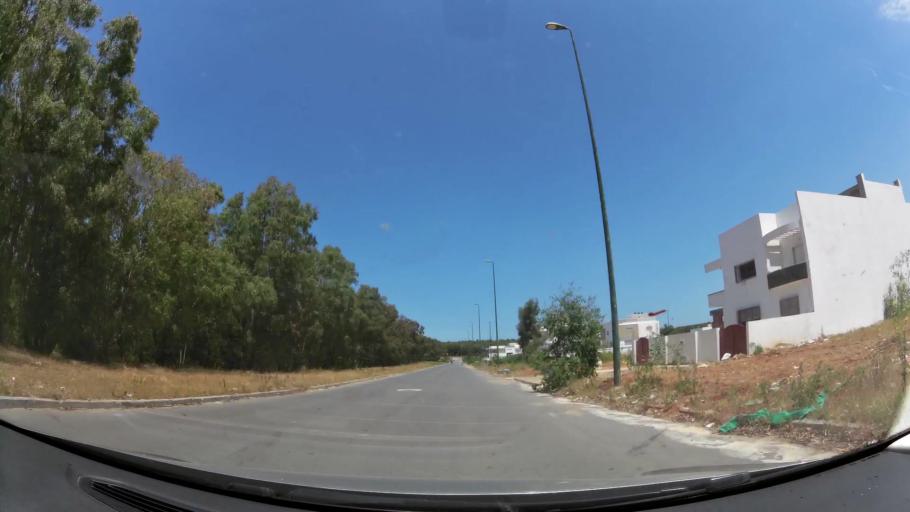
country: MA
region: Gharb-Chrarda-Beni Hssen
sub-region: Kenitra Province
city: Kenitra
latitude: 34.2673
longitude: -6.6317
